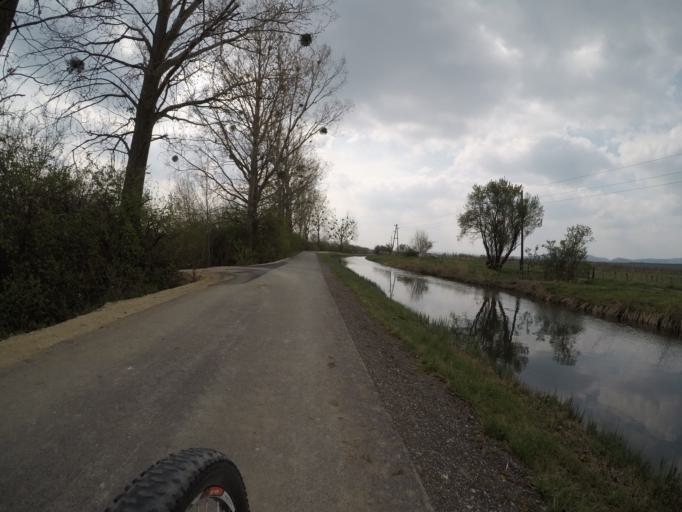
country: AT
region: Lower Austria
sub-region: Politischer Bezirk Baden
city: Baden
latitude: 47.9865
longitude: 16.2549
